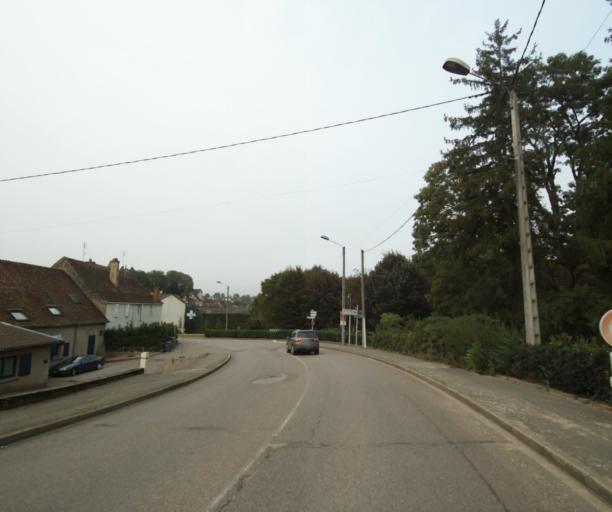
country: FR
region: Bourgogne
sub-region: Departement de Saone-et-Loire
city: Charolles
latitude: 46.4373
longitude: 4.2805
